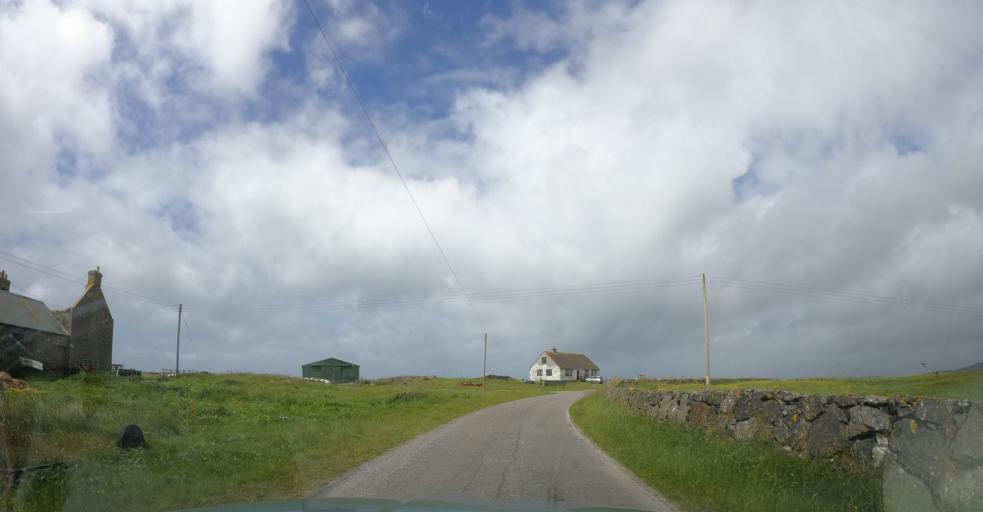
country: GB
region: Scotland
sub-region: Eilean Siar
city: Isle of South Uist
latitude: 57.2608
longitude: -7.4079
